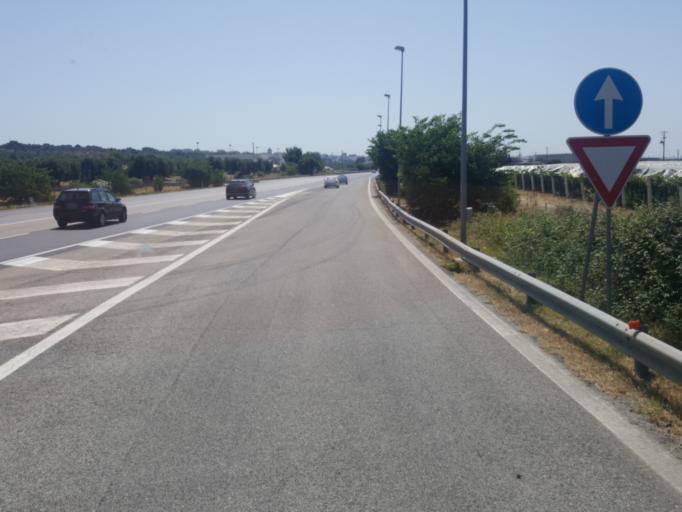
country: IT
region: Apulia
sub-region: Provincia di Taranto
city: Massafra
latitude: 40.5962
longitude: 17.0851
